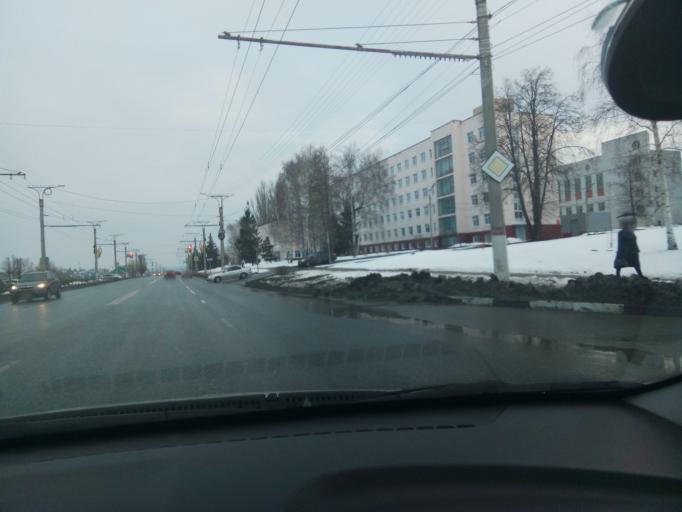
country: RU
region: Chuvashia
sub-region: Cheboksarskiy Rayon
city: Cheboksary
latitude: 56.1381
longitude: 47.2431
